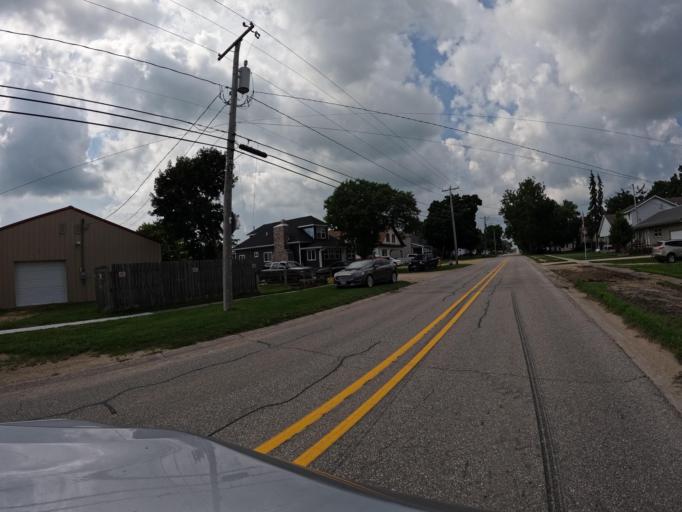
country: US
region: Iowa
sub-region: Clinton County
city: Camanche
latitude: 41.7985
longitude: -90.3550
